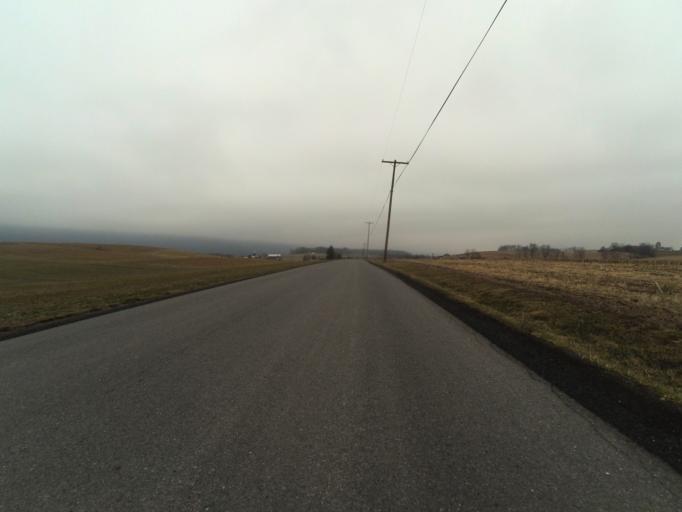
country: US
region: Pennsylvania
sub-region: Centre County
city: Centre Hall
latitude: 40.8507
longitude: -77.6546
